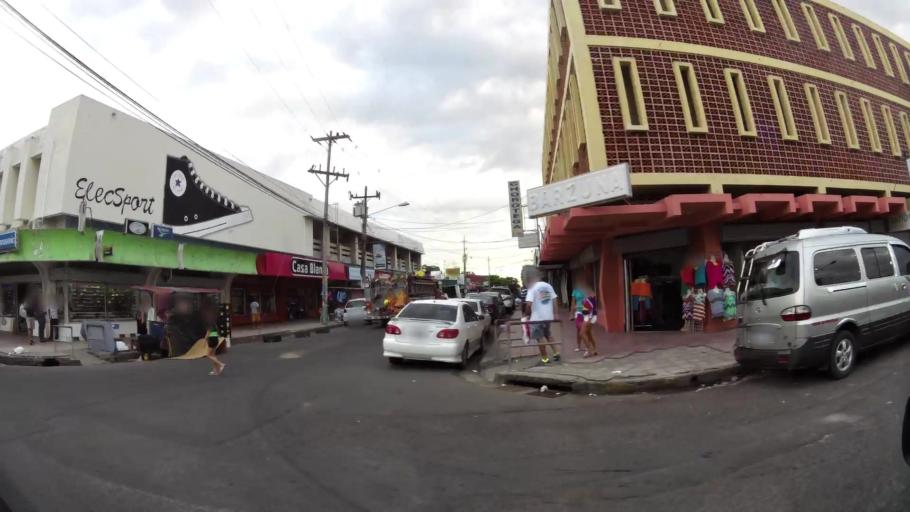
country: CR
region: Puntarenas
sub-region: Canton Central de Puntarenas
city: Puntarenas
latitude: 9.9794
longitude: -84.8329
